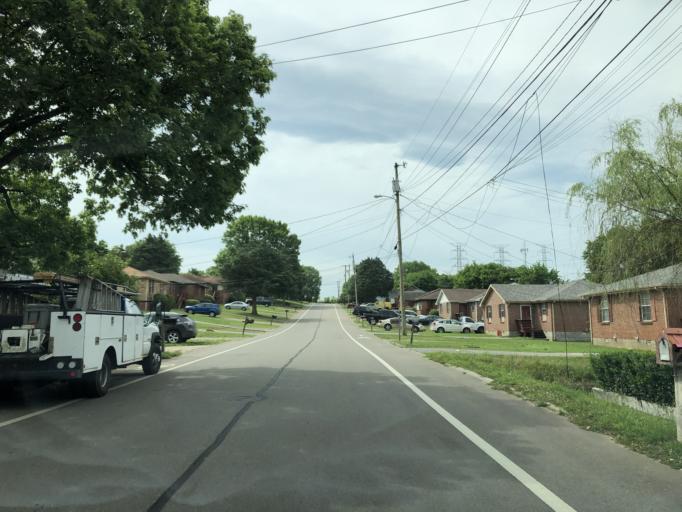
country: US
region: Tennessee
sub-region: Davidson County
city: Goodlettsville
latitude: 36.2839
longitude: -86.7148
